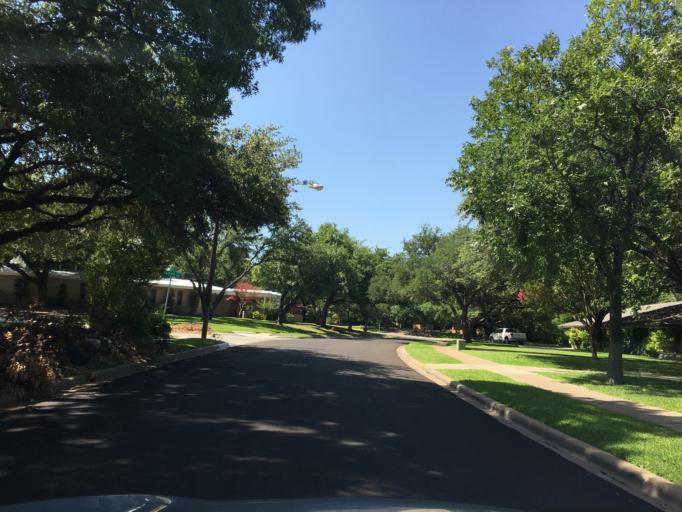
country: US
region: Texas
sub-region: Dallas County
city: University Park
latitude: 32.9029
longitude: -96.7861
